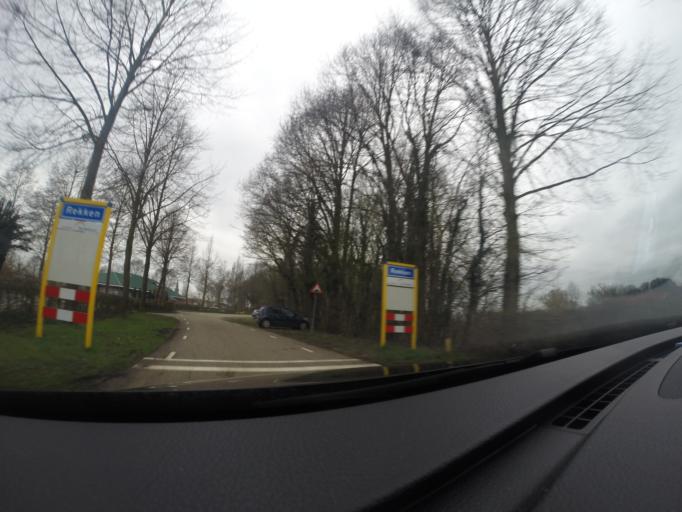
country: NL
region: Overijssel
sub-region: Gemeente Haaksbergen
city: Haaksbergen
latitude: 52.0927
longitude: 6.7198
